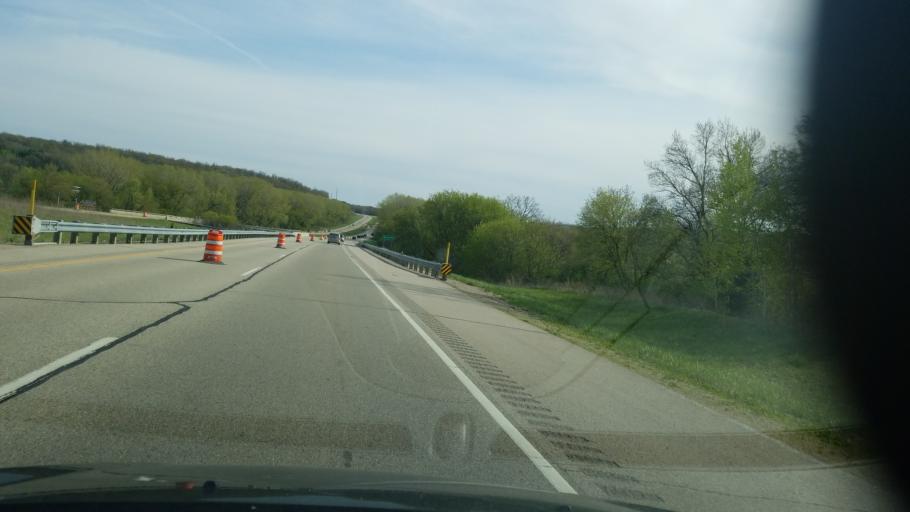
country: US
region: Wisconsin
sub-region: Dane County
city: Oregon
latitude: 42.9727
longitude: -89.3866
